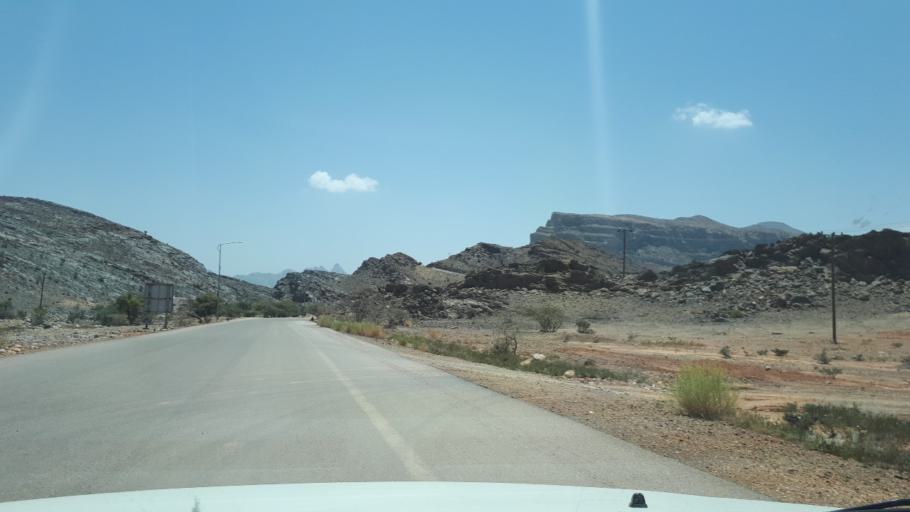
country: OM
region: Muhafazat ad Dakhiliyah
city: Bahla'
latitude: 23.2401
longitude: 57.1498
